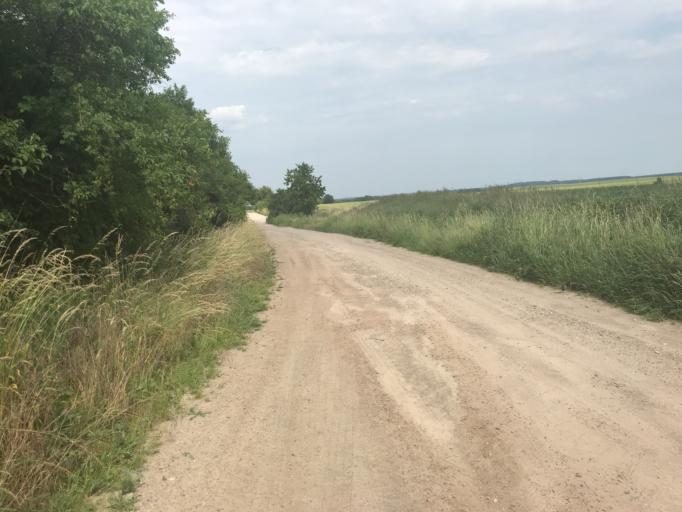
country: PL
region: West Pomeranian Voivodeship
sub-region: Powiat gryfinski
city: Chojna
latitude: 52.9219
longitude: 14.4360
